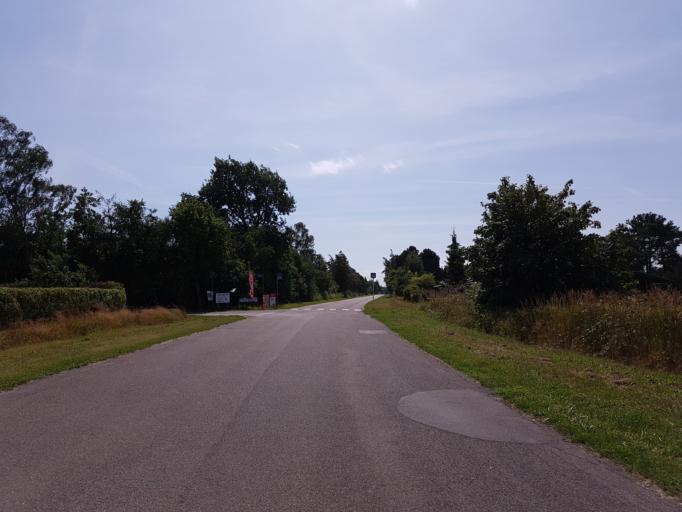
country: DK
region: Zealand
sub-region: Guldborgsund Kommune
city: Nykobing Falster
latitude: 54.5974
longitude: 11.9648
